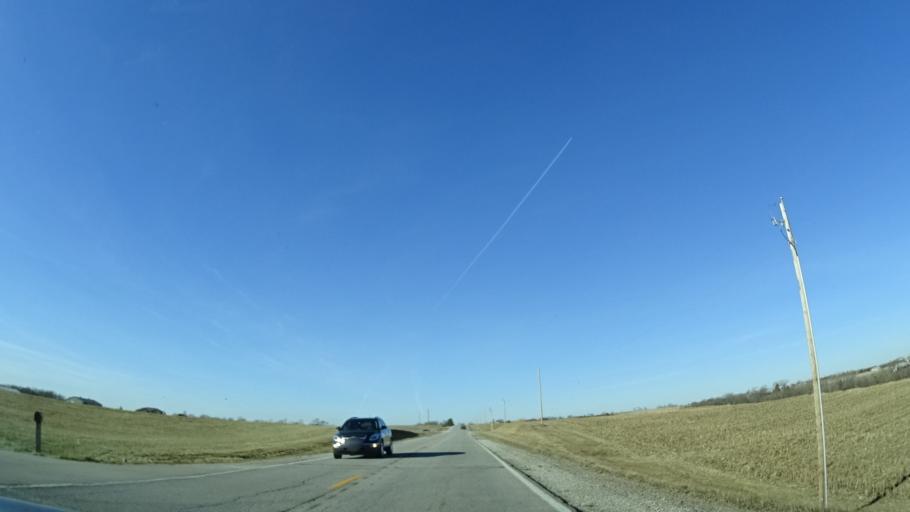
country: US
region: Nebraska
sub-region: Sarpy County
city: Papillion
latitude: 41.0887
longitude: -96.0525
